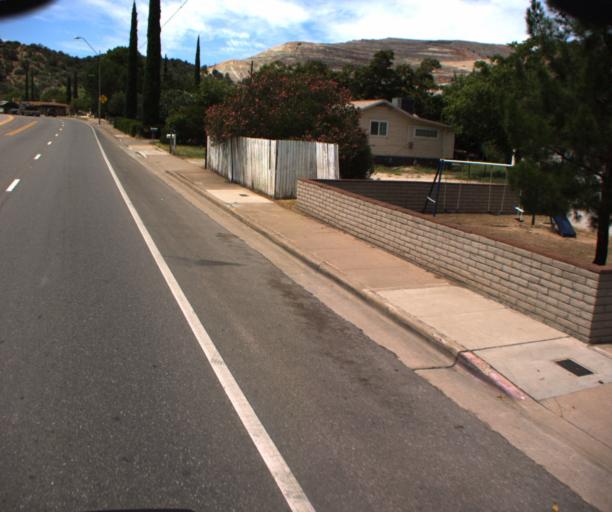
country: US
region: Arizona
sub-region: Gila County
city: Miami
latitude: 33.3948
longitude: -110.8767
